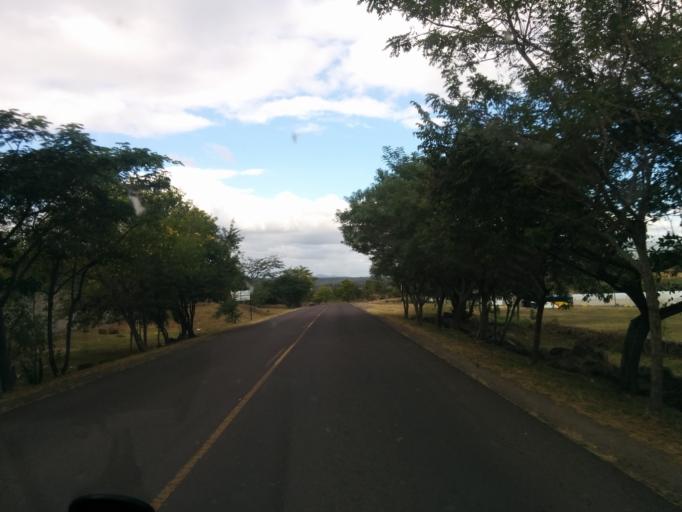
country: NI
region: Esteli
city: Esteli
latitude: 13.1708
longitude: -86.3668
